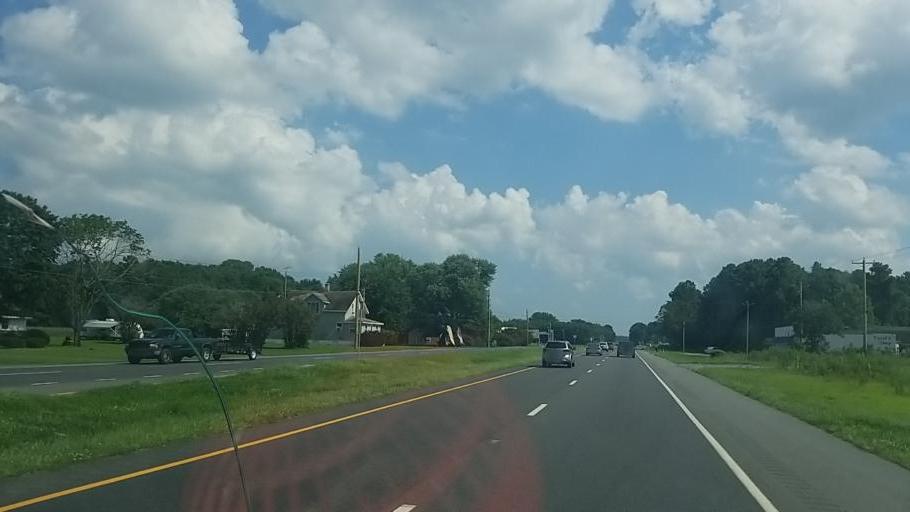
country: US
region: Delaware
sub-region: Sussex County
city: Millsboro
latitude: 38.5370
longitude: -75.2542
